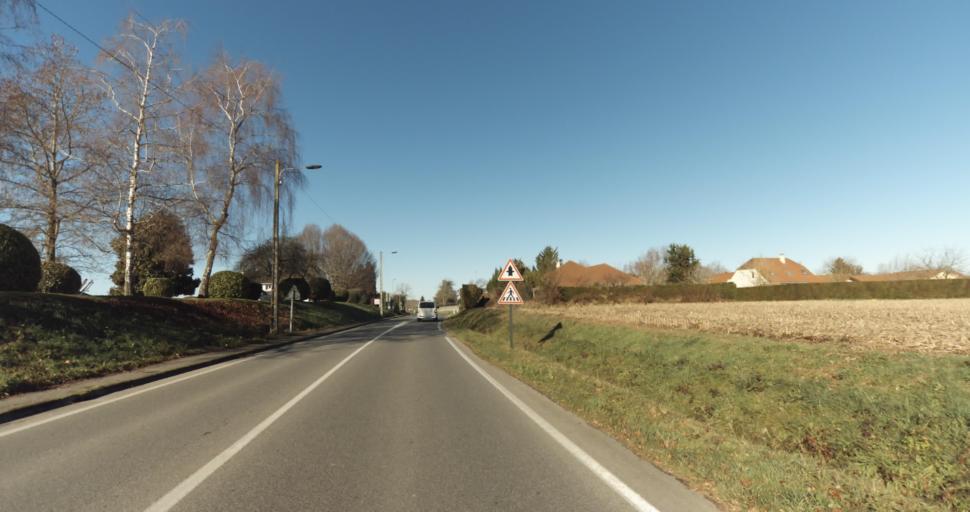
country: FR
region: Aquitaine
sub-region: Departement des Pyrenees-Atlantiques
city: Morlaas
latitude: 43.3513
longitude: -0.2645
